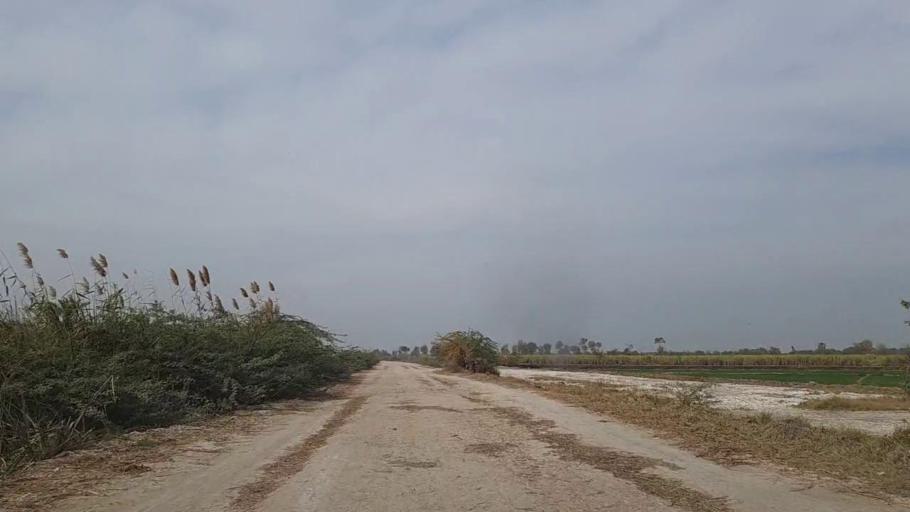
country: PK
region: Sindh
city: Daur
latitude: 26.4043
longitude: 68.4380
